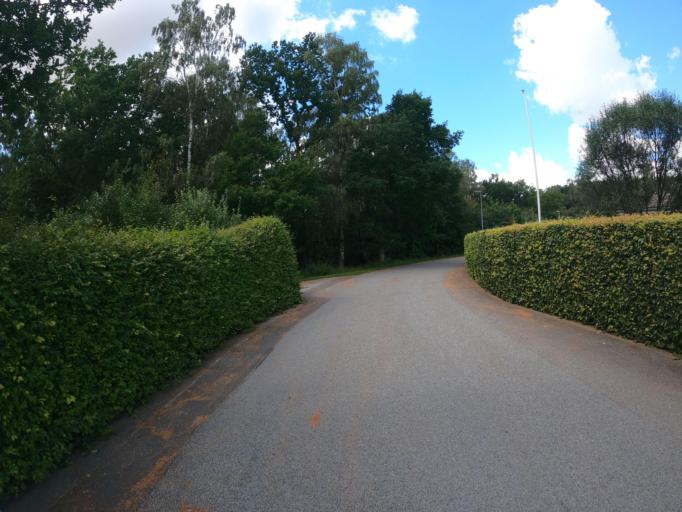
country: SE
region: Skane
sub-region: Lunds Kommun
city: Genarp
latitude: 55.6770
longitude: 13.3463
